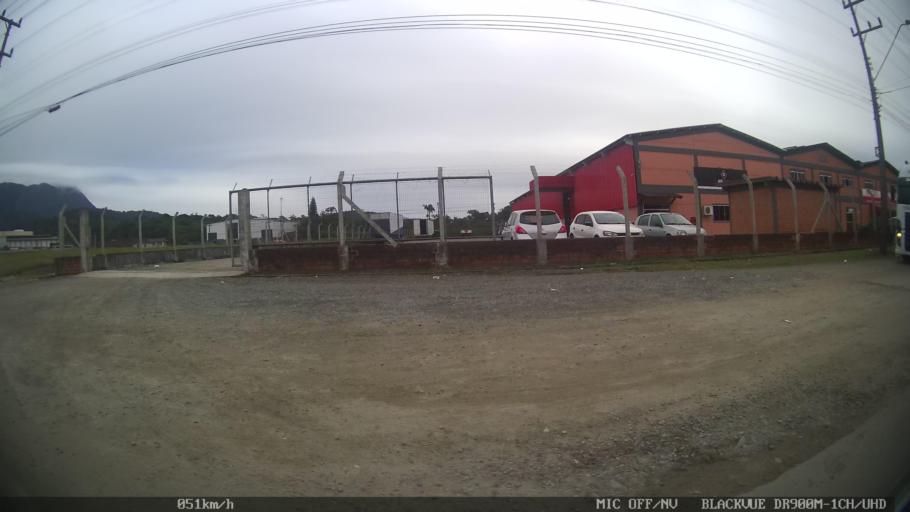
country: BR
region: Santa Catarina
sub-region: Joinville
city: Joinville
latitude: -26.2313
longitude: -48.9008
